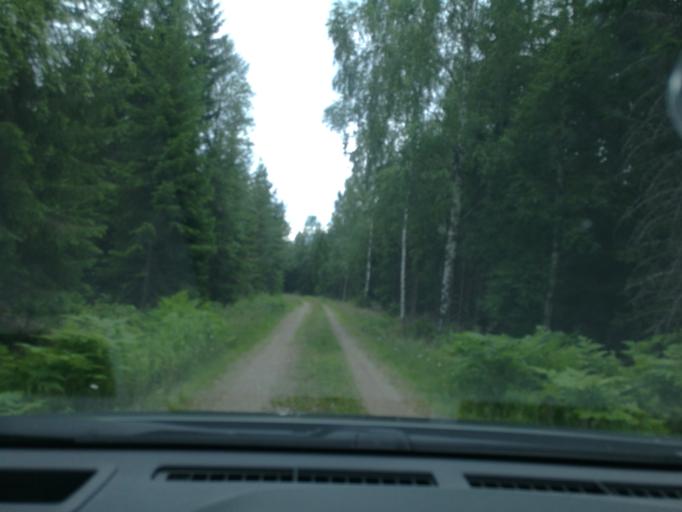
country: SE
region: Vaestmanland
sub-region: Surahammars Kommun
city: Ramnas
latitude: 59.8068
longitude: 16.3180
